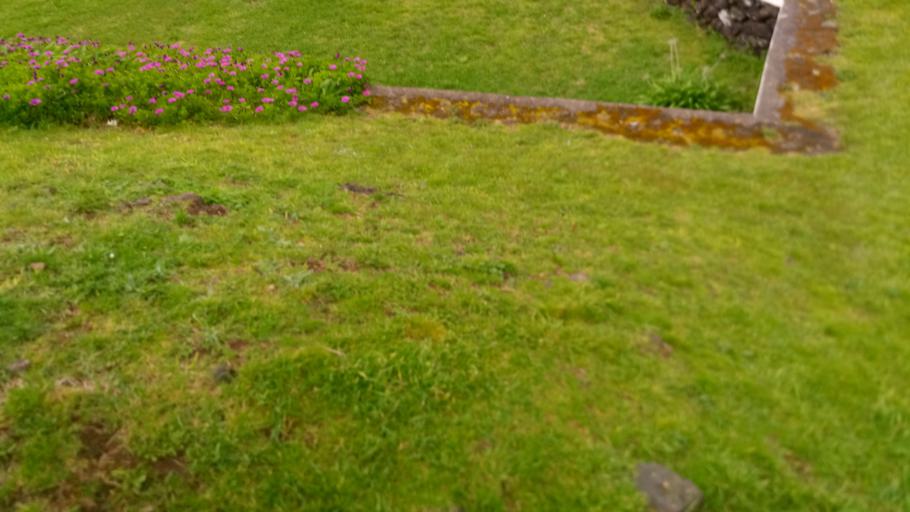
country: PT
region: Azores
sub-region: Praia da Vitoria
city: Biscoitos
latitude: 38.7803
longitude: -27.3575
